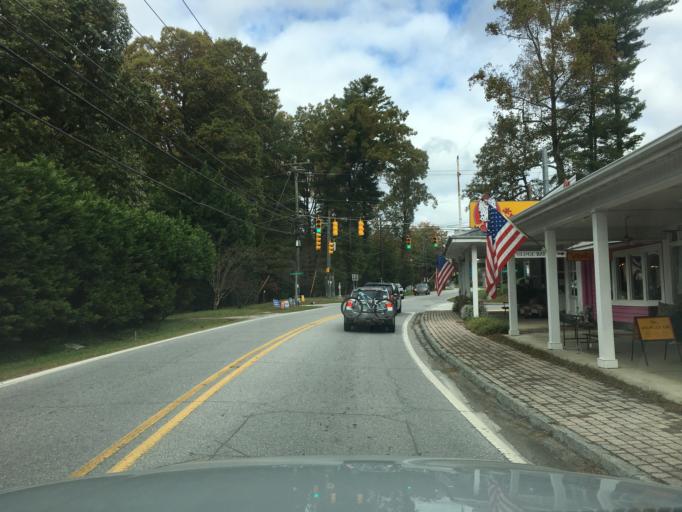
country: US
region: North Carolina
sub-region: Henderson County
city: Flat Rock
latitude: 35.2707
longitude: -82.4414
